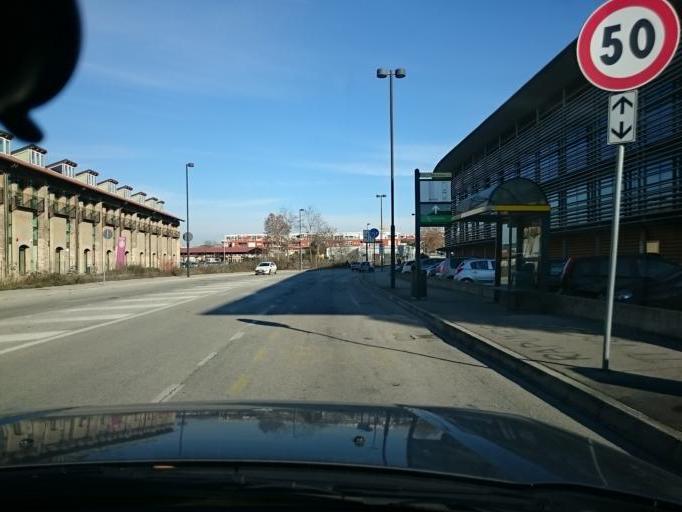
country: IT
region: Veneto
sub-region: Provincia di Venezia
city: Mestre
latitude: 45.4842
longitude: 12.2508
